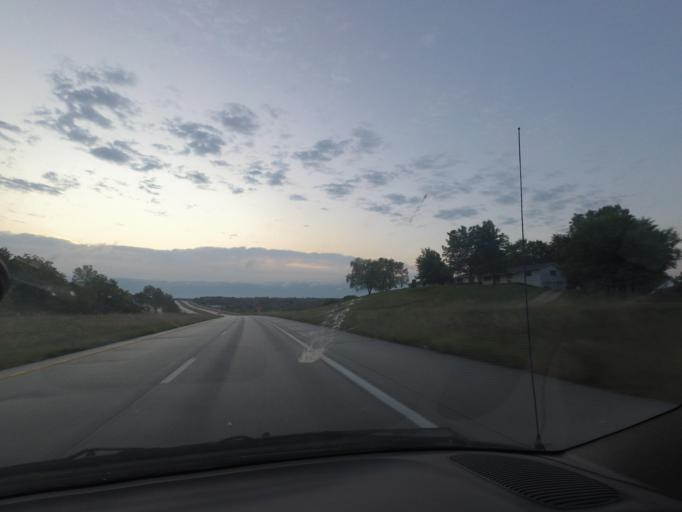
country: US
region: Missouri
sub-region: Macon County
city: Macon
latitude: 39.7496
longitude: -92.5251
